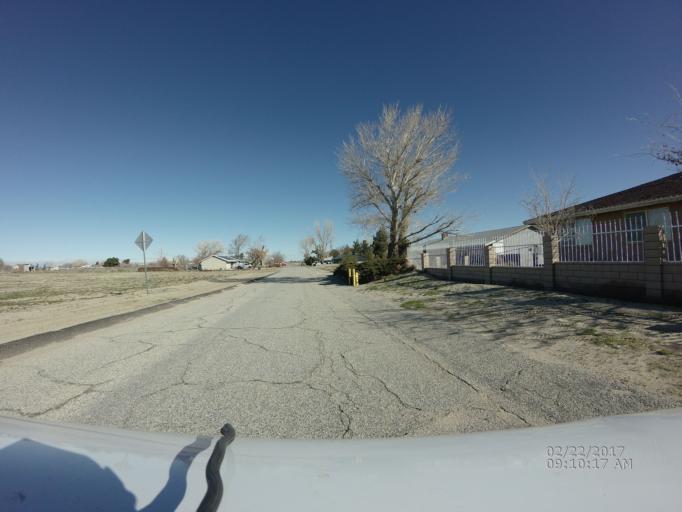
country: US
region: California
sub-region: Los Angeles County
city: Lake Los Angeles
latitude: 34.6195
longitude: -117.8581
